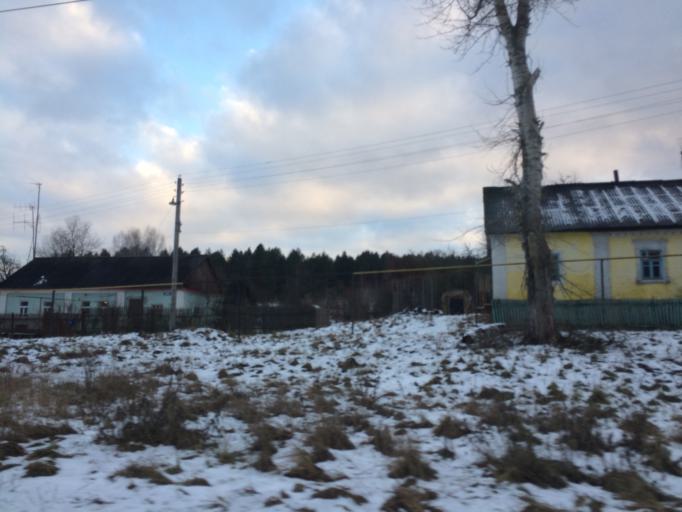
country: RU
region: Tula
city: Cherepet'
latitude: 54.1155
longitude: 36.3525
